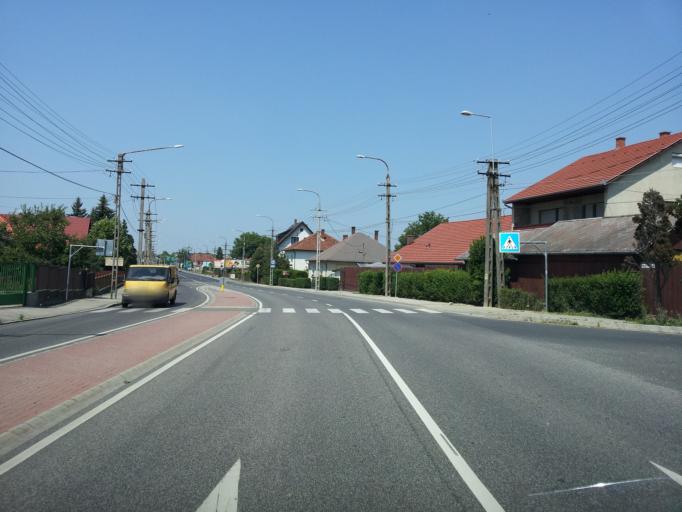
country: HU
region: Zala
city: Zalaegerszeg
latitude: 46.8422
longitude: 16.8763
